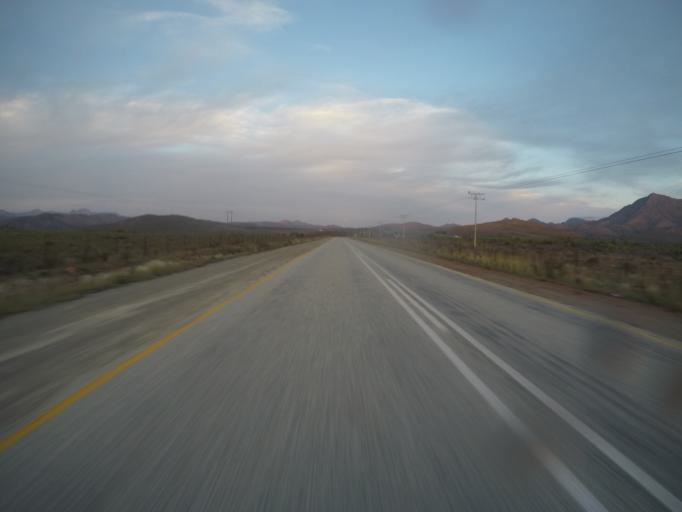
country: ZA
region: Western Cape
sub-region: Eden District Municipality
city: Plettenberg Bay
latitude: -33.7301
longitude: 23.3938
